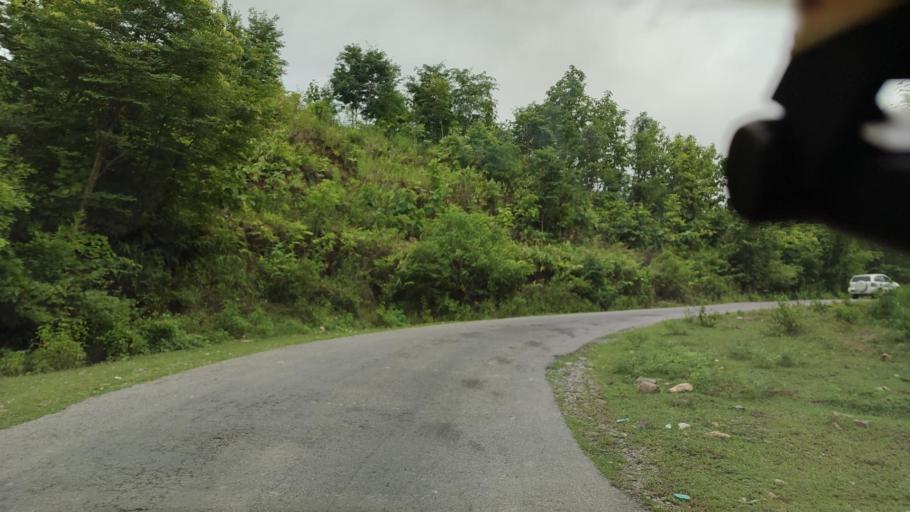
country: MM
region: Mandalay
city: Nay Pyi Taw
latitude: 19.9934
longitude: 95.9080
